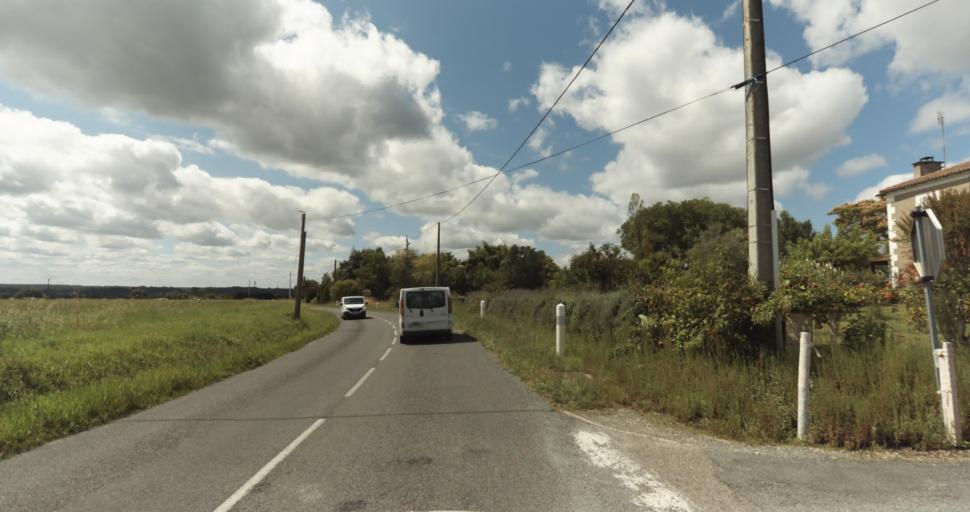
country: FR
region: Aquitaine
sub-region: Departement de la Gironde
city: Bazas
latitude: 44.4463
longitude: -0.2067
